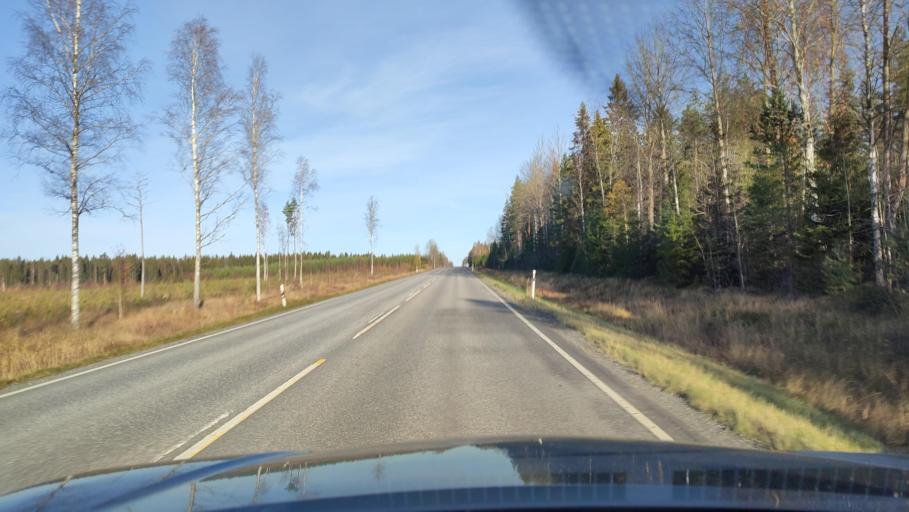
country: FI
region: Ostrobothnia
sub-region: Sydosterbotten
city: Naerpes
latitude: 62.4956
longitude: 21.4463
